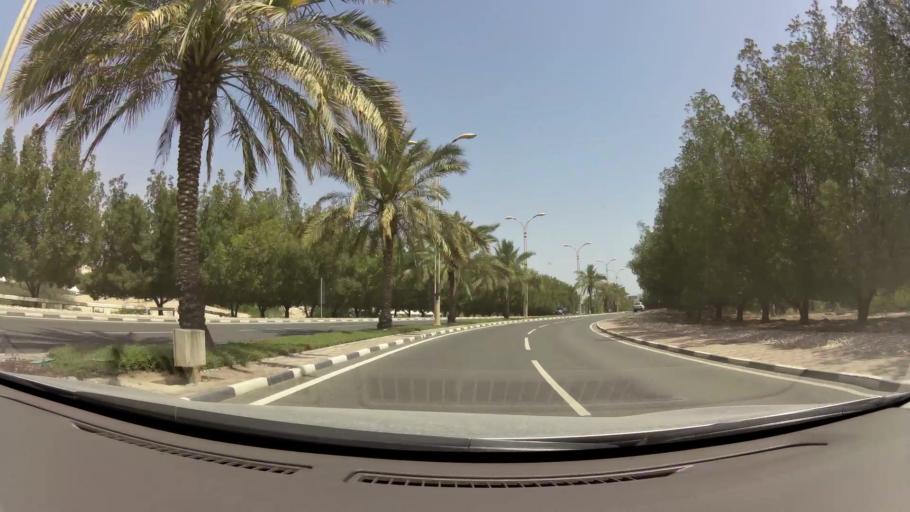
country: QA
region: Baladiyat ad Dawhah
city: Doha
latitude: 25.3709
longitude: 51.4937
